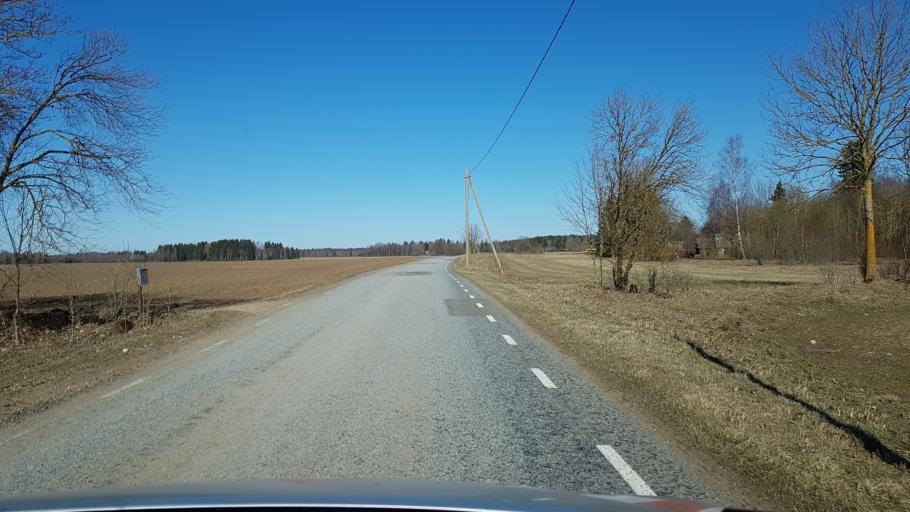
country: EE
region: Laeaene-Virumaa
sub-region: Someru vald
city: Someru
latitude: 59.3776
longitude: 26.4565
